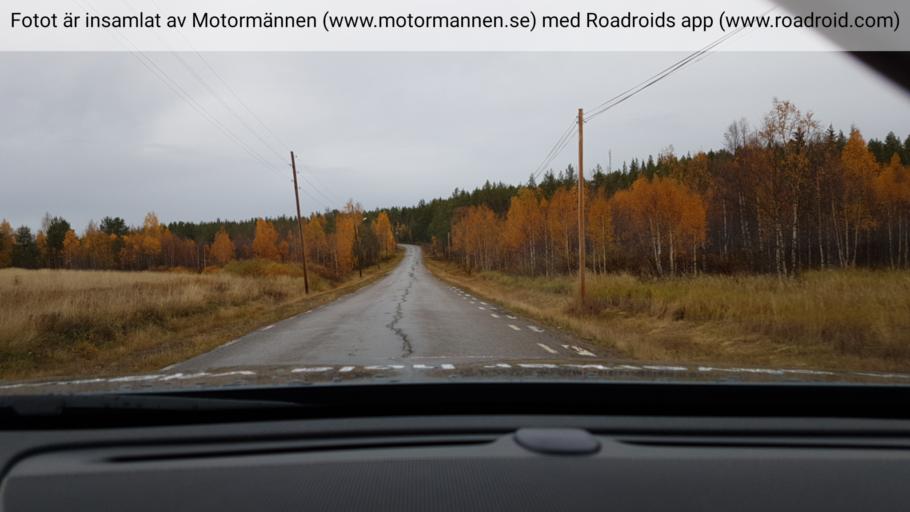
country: SE
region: Norrbotten
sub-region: Pajala Kommun
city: Pajala
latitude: 67.1469
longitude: 22.6524
